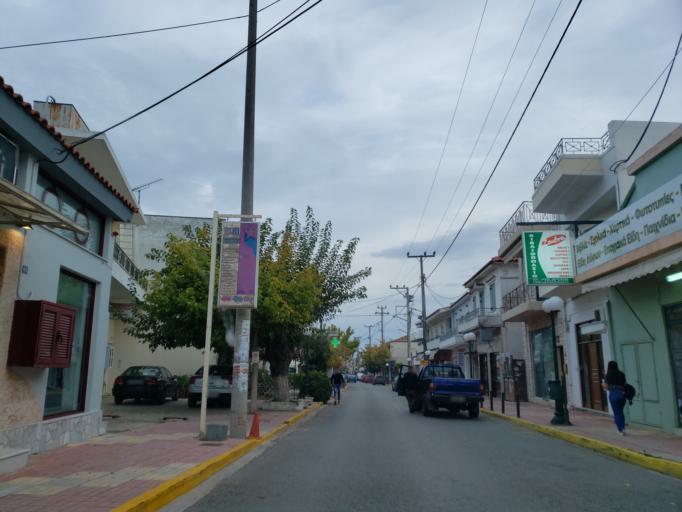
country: GR
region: Attica
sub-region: Nomarchia Anatolikis Attikis
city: Marathonas
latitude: 38.1572
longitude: 23.9595
